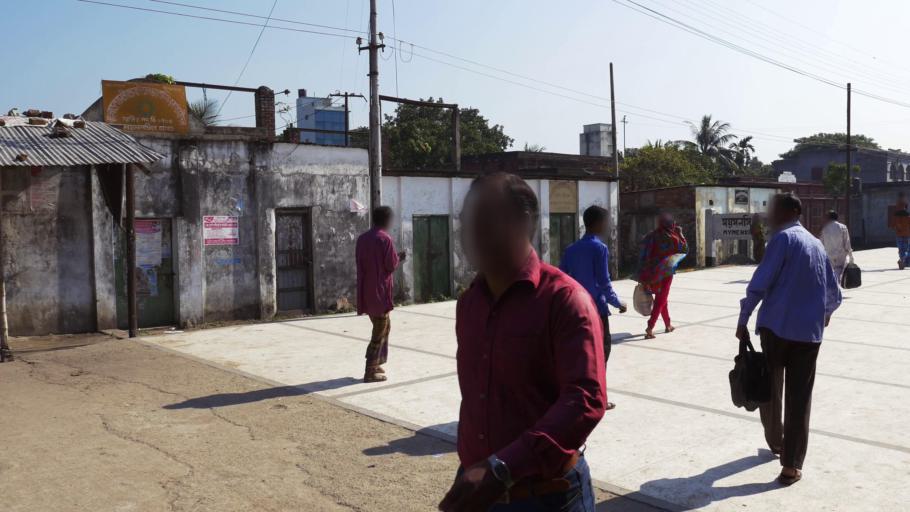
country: BD
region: Dhaka
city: Mymensingh
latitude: 24.6989
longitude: 90.4502
